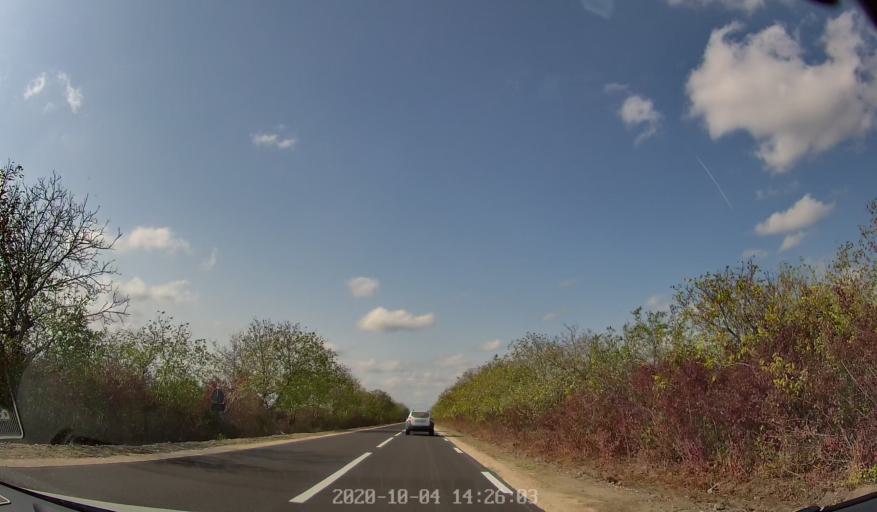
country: MD
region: Rezina
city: Saharna
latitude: 47.6241
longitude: 28.8904
